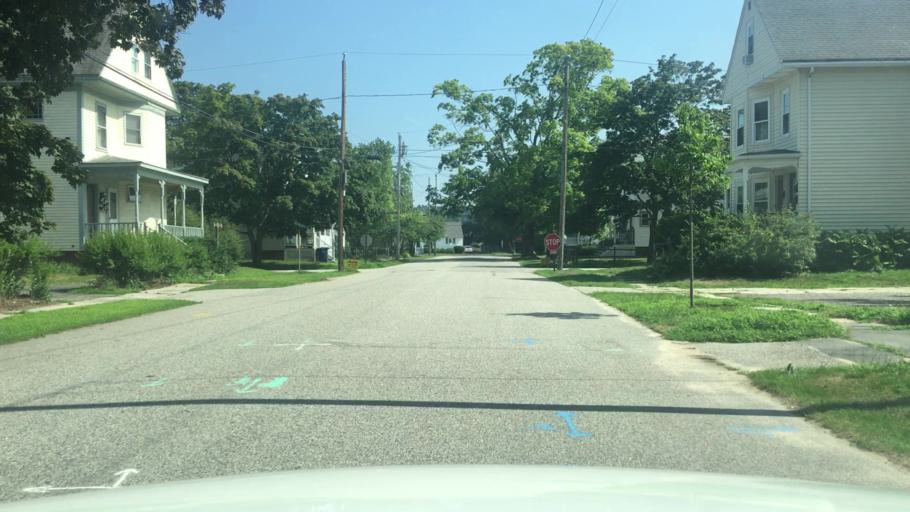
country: US
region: Maine
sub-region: Cumberland County
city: South Portland
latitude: 43.6312
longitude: -70.2714
